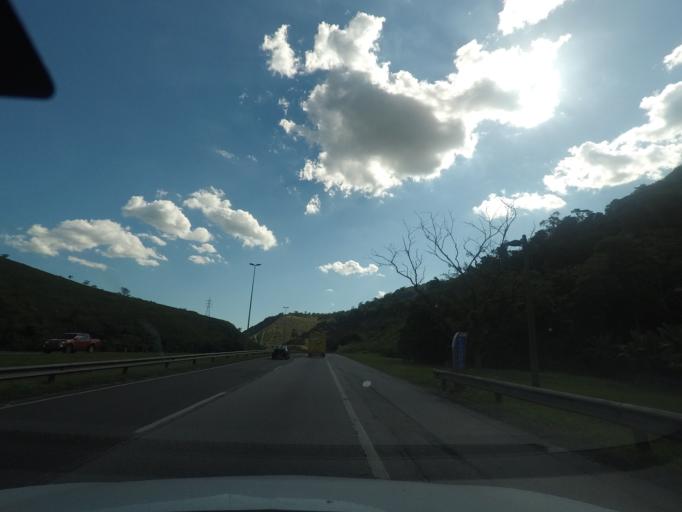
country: BR
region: Rio de Janeiro
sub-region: Guapimirim
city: Guapimirim
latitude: -22.5714
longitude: -43.0068
